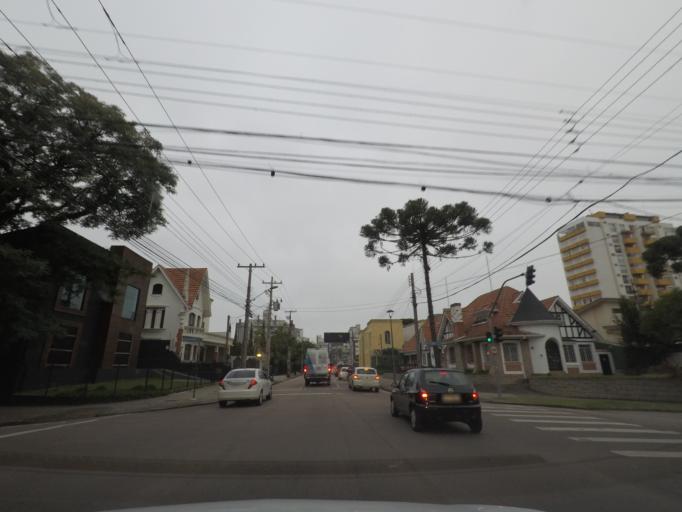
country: BR
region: Parana
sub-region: Curitiba
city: Curitiba
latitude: -25.4279
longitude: -49.2586
